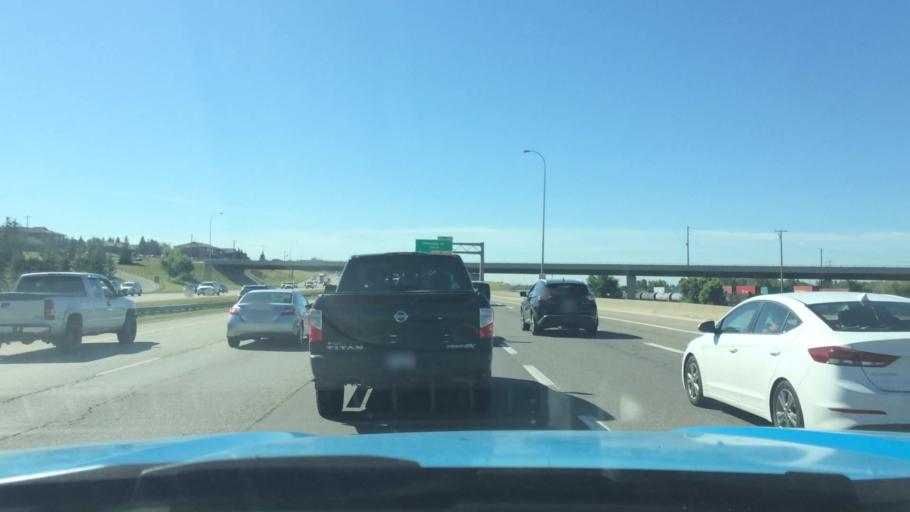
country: CA
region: Alberta
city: Calgary
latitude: 51.0615
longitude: -114.0257
